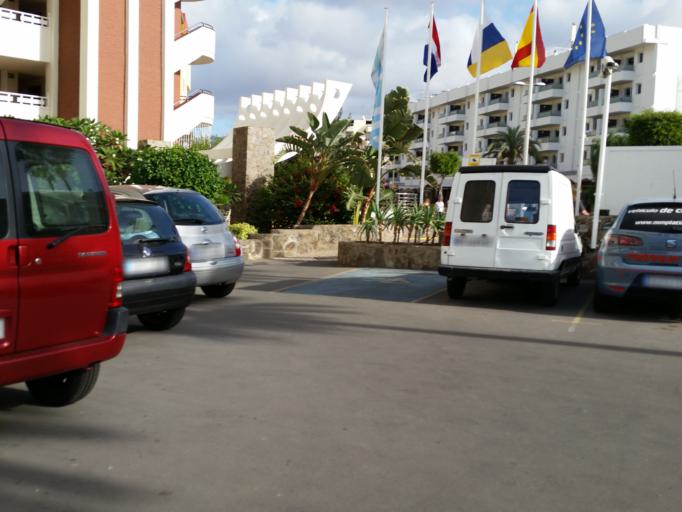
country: ES
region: Canary Islands
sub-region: Provincia de Las Palmas
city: Playa del Ingles
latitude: 27.7603
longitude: -15.5792
